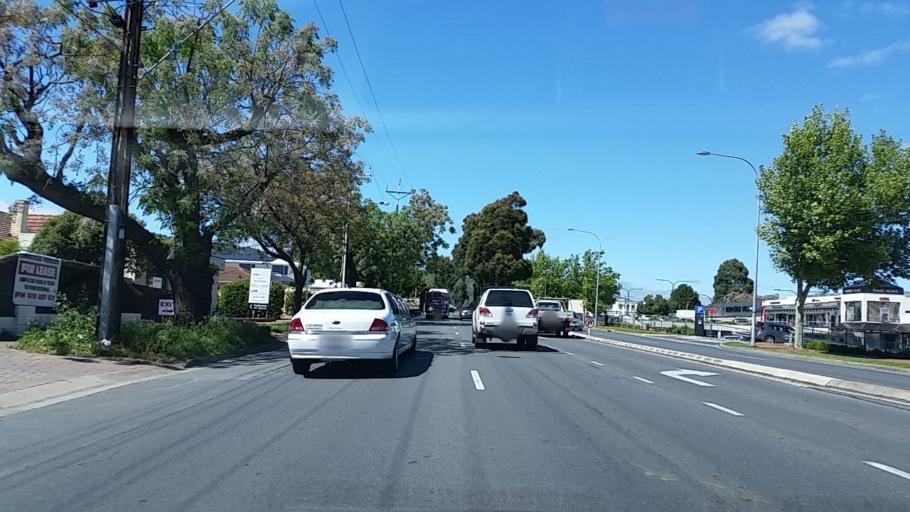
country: AU
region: South Australia
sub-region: Burnside
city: Tusmore
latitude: -34.9407
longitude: 138.6426
